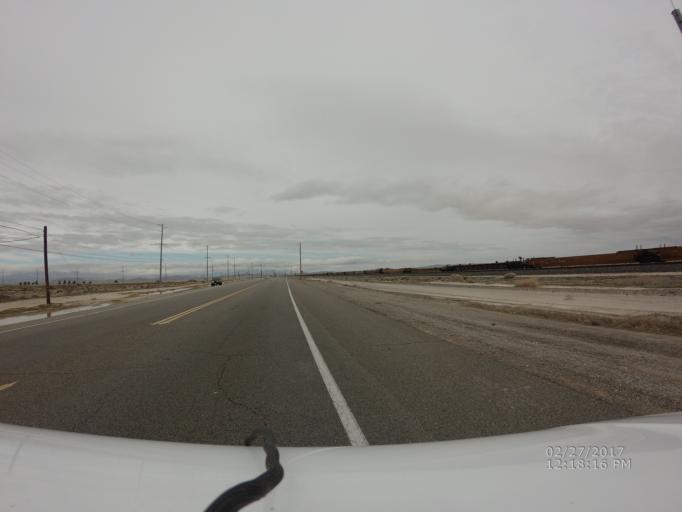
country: US
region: California
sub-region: Los Angeles County
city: Lancaster
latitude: 34.7753
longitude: -118.1490
